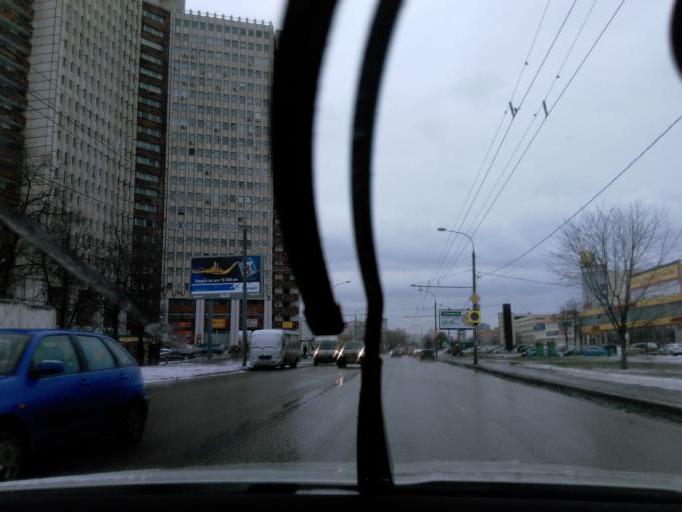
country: RU
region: Moscow
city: Zapadnoye Degunino
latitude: 55.8659
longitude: 37.5437
